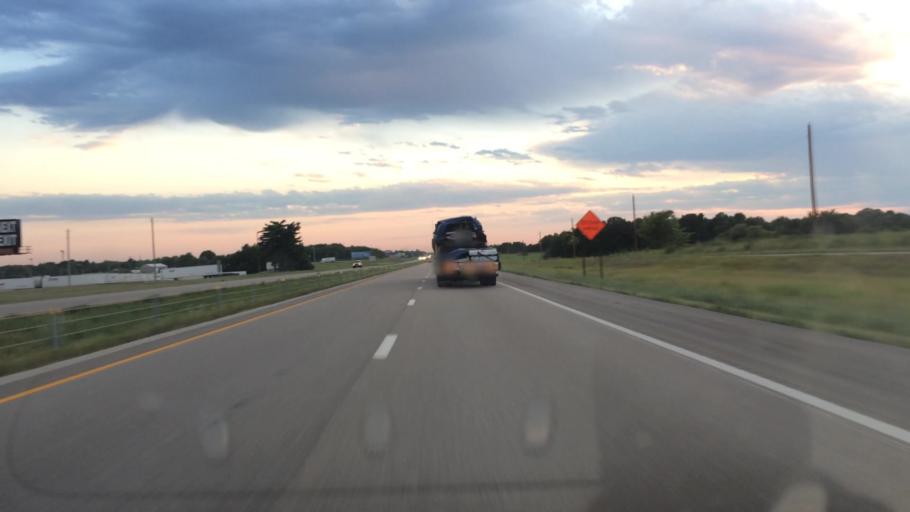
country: US
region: Missouri
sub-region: Greene County
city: Strafford
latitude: 37.2622
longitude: -93.1487
